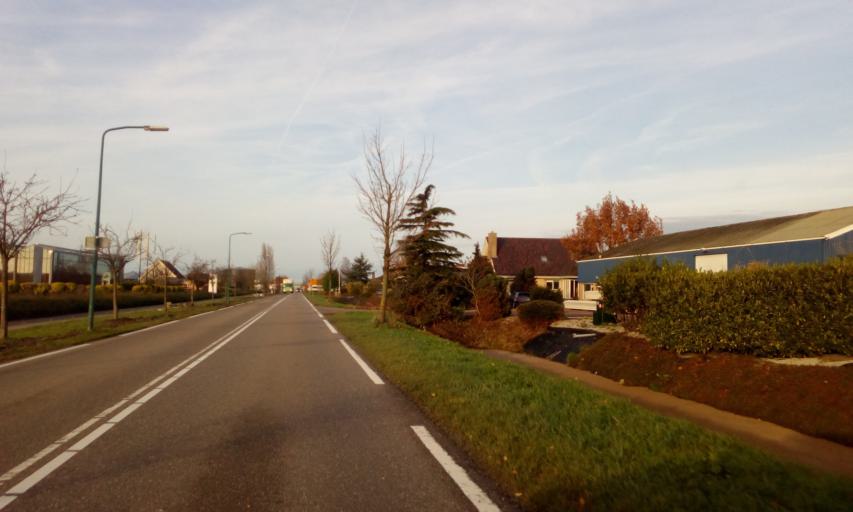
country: NL
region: South Holland
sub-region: Gemeente Lansingerland
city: Bleiswijk
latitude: 52.0215
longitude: 4.5256
